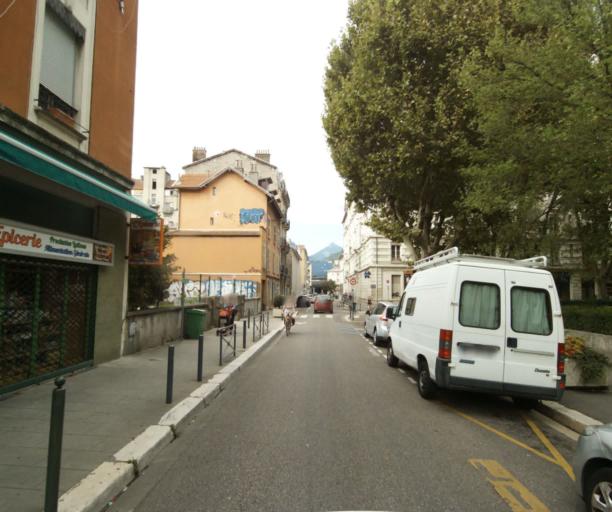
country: FR
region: Rhone-Alpes
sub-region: Departement de l'Isere
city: Saint-Martin-le-Vinoux
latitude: 45.1874
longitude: 5.7125
